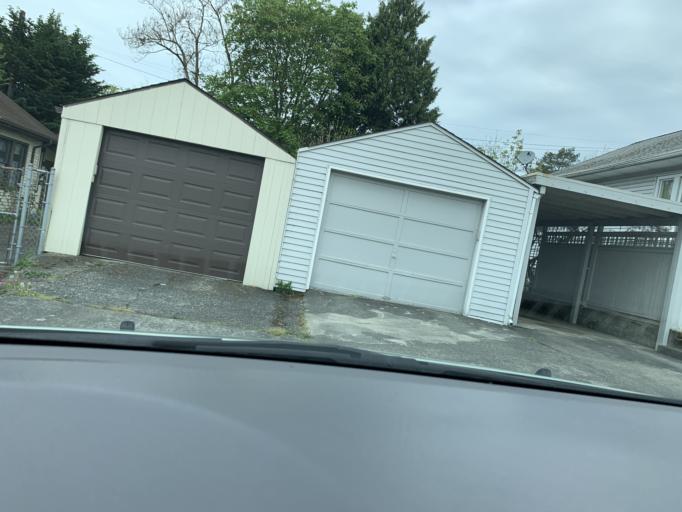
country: US
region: Washington
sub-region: King County
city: Seattle
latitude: 47.5542
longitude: -122.3136
